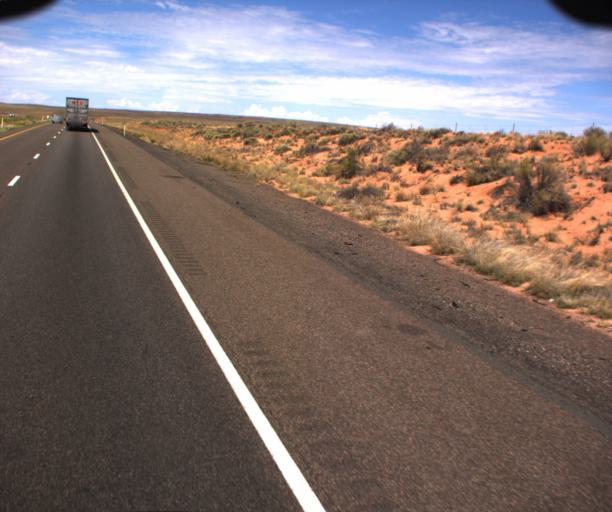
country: US
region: Arizona
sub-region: Navajo County
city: Holbrook
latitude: 35.0812
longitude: -109.7192
